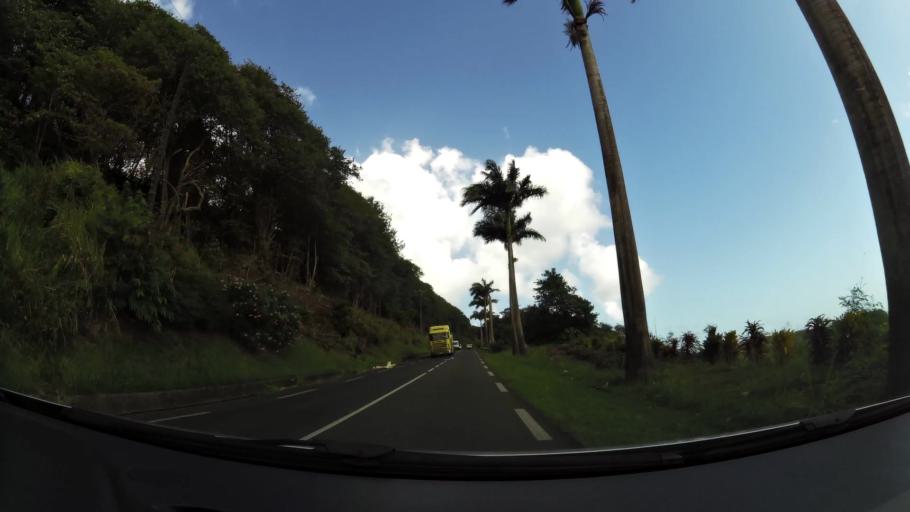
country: MQ
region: Martinique
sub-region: Martinique
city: Le Lorrain
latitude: 14.8281
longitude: -61.0427
